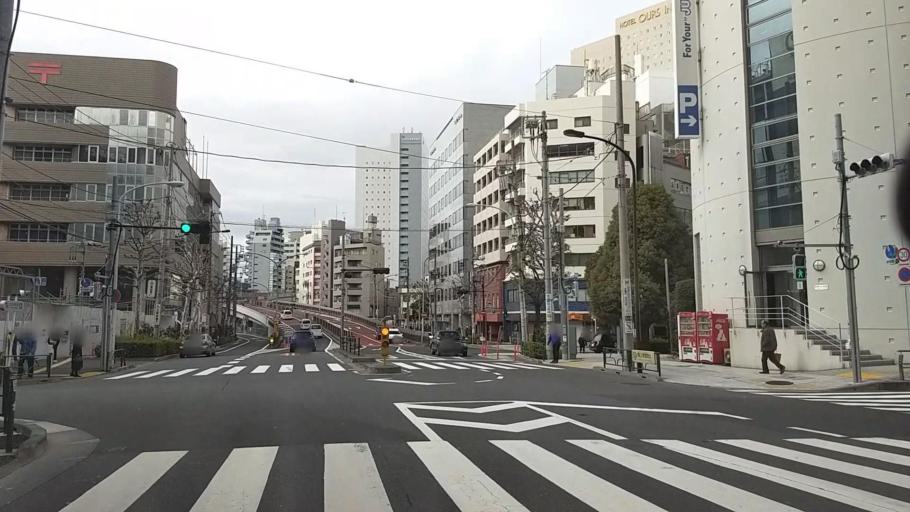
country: JP
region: Kanagawa
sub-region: Kawasaki-shi
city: Kawasaki
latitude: 35.6059
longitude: 139.7368
